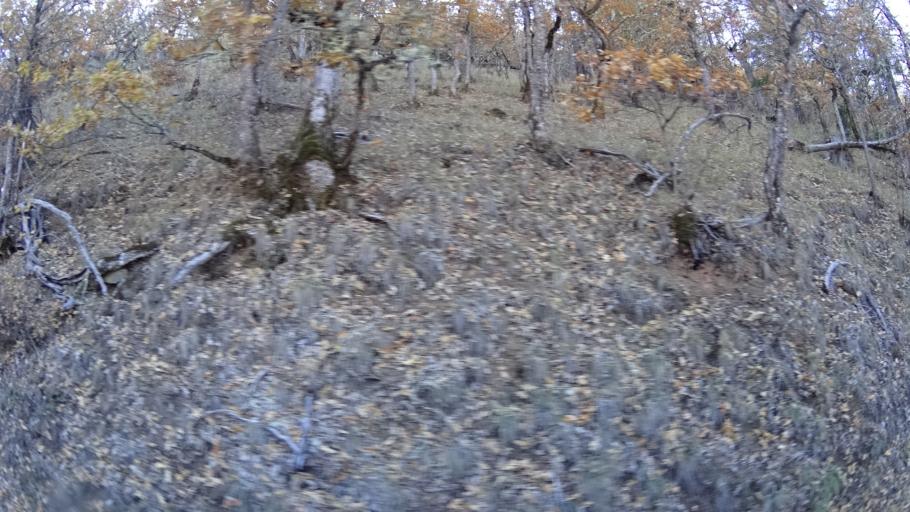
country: US
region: California
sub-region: Siskiyou County
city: Yreka
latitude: 41.8672
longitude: -122.8126
